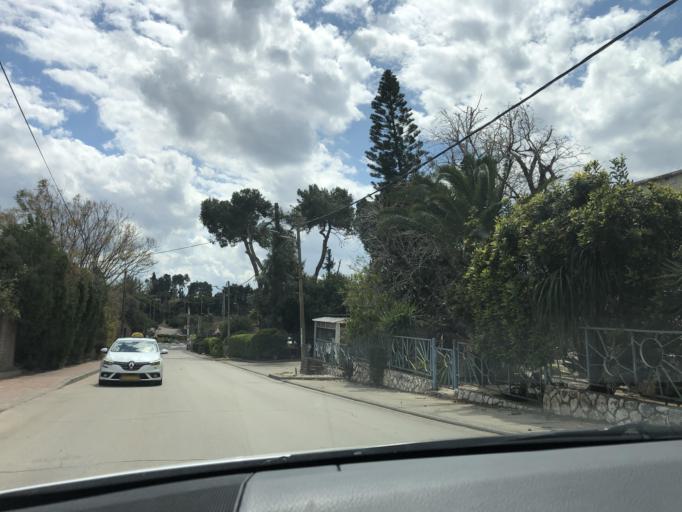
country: IL
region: Central District
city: Tel Mond
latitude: 32.2626
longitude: 34.9301
